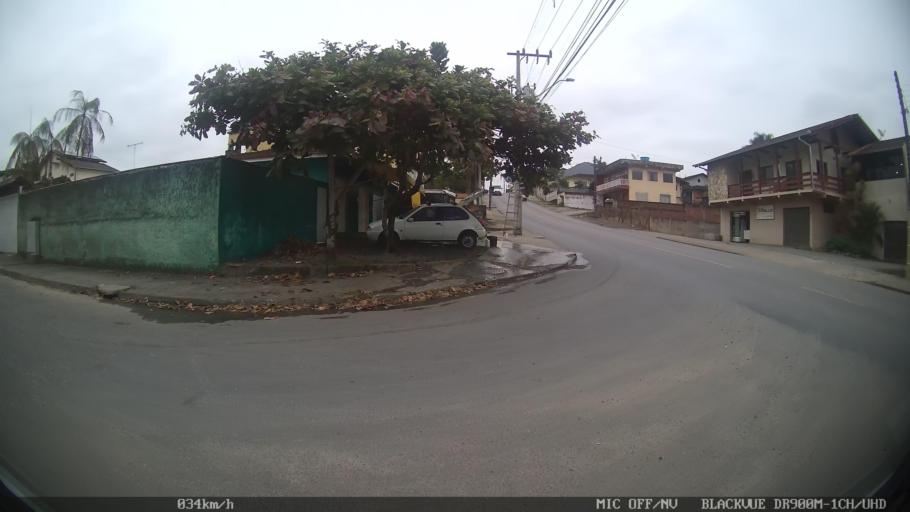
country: BR
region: Santa Catarina
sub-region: Joinville
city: Joinville
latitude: -26.3655
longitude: -48.8241
